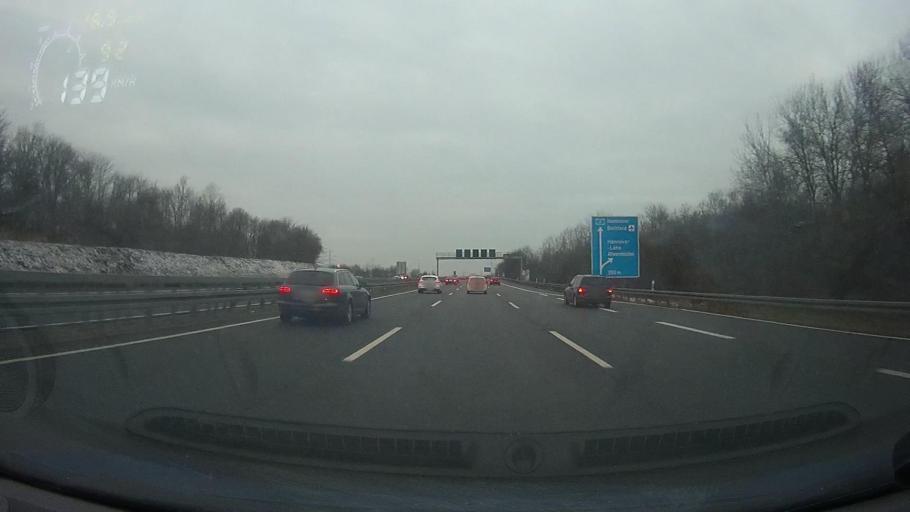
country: DE
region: Lower Saxony
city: Isernhagen Farster Bauerschaft
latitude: 52.4169
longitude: 9.8407
